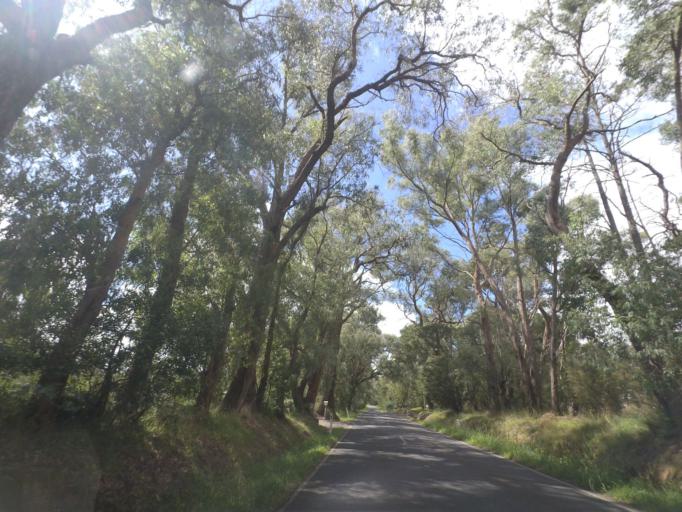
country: AU
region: Victoria
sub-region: Yarra Ranges
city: Launching Place
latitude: -37.7884
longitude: 145.5670
